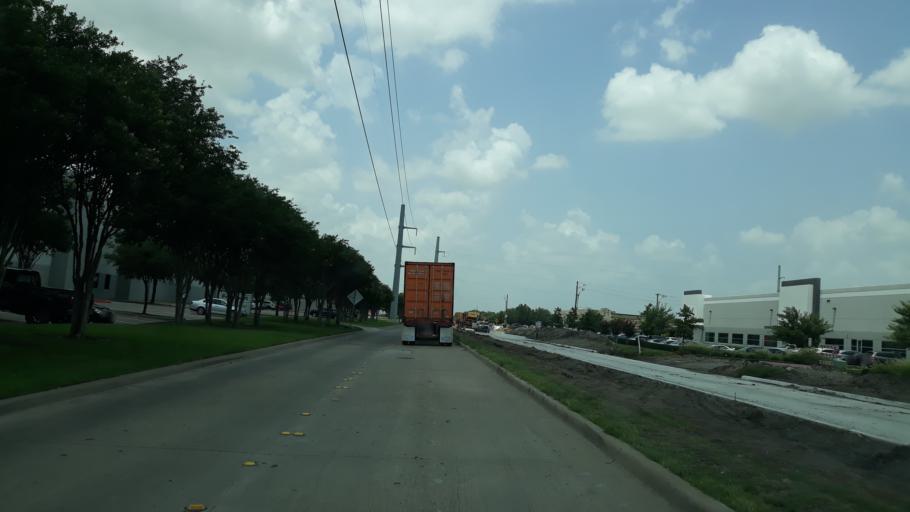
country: US
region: Texas
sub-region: Dallas County
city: Coppell
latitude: 32.9468
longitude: -97.0111
